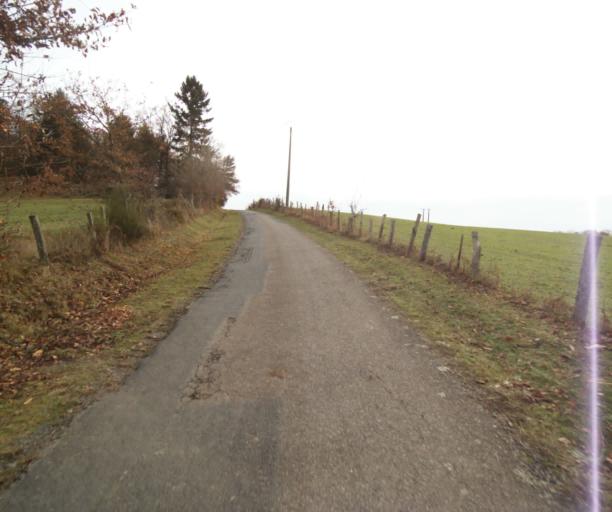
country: FR
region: Limousin
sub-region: Departement de la Correze
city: Saint-Mexant
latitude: 45.2583
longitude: 1.6485
